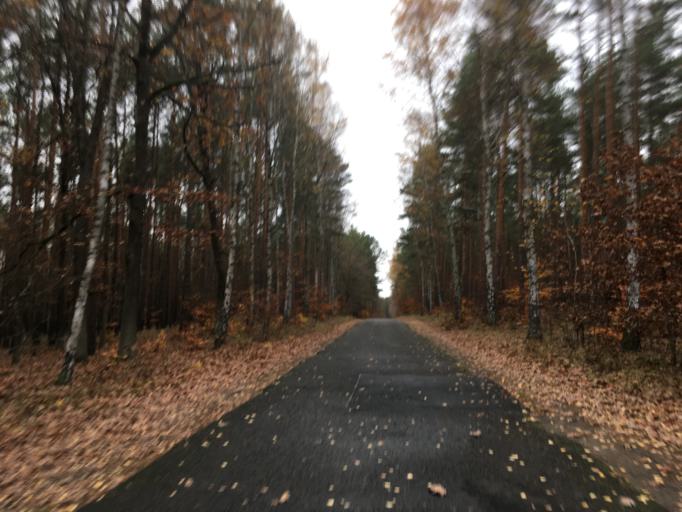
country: DE
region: Brandenburg
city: Mixdorf
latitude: 52.1786
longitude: 14.4343
